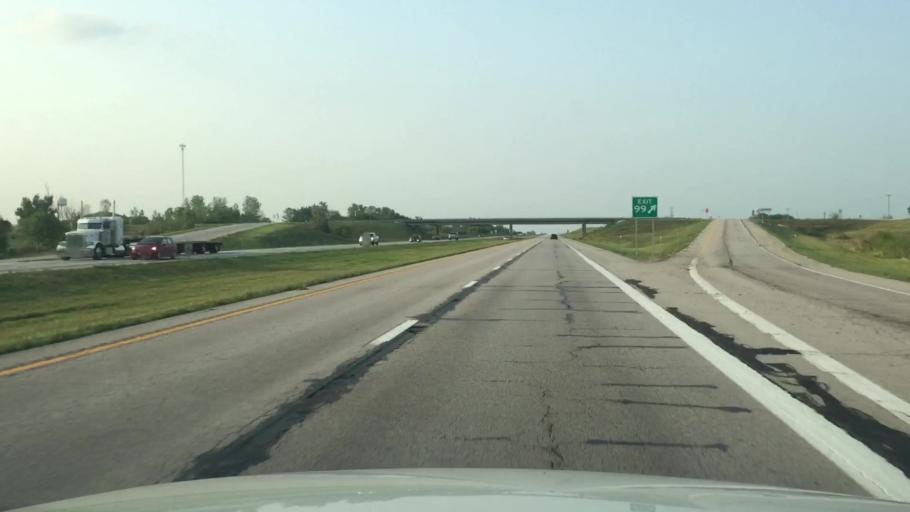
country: US
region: Missouri
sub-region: Harrison County
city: Bethany
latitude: 40.3714
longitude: -94.0036
